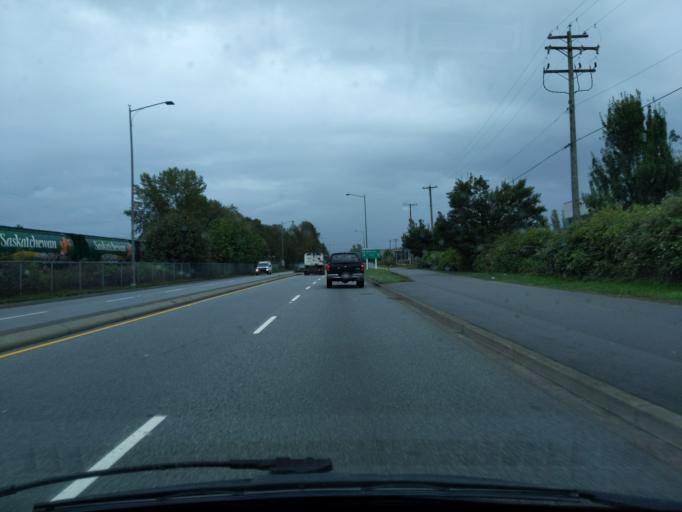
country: CA
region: British Columbia
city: Pitt Meadows
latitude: 49.1807
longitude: -122.7004
